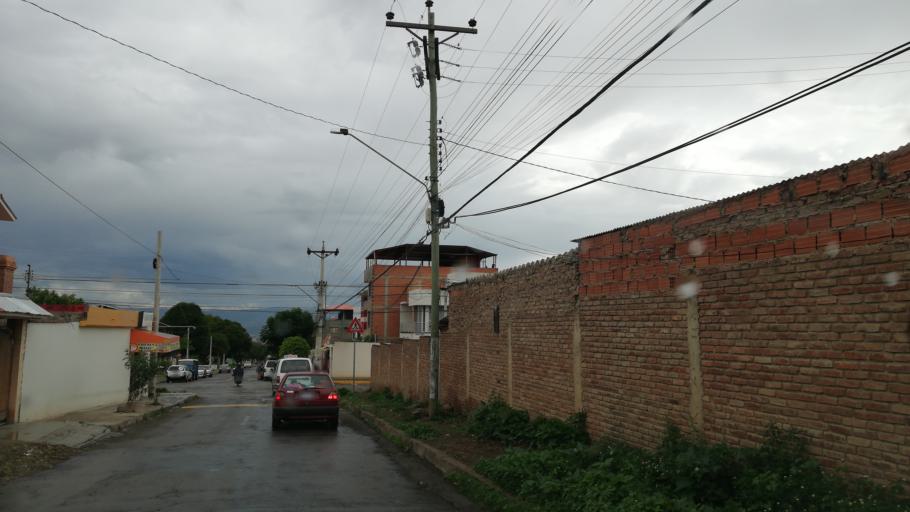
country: BO
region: Cochabamba
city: Cochabamba
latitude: -17.3501
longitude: -66.1800
